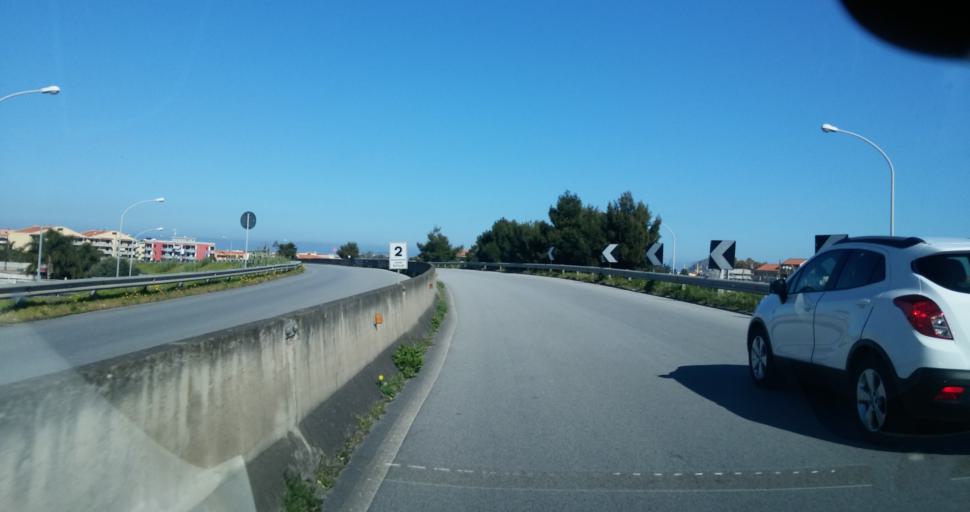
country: IT
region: Sicily
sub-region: Messina
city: Milazzo
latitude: 38.2047
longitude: 15.2460
